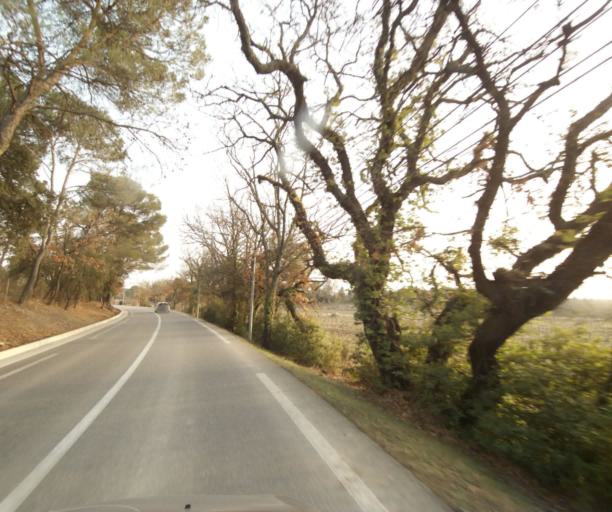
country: FR
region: Provence-Alpes-Cote d'Azur
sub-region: Departement des Bouches-du-Rhone
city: Rognes
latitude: 43.6399
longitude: 5.3590
